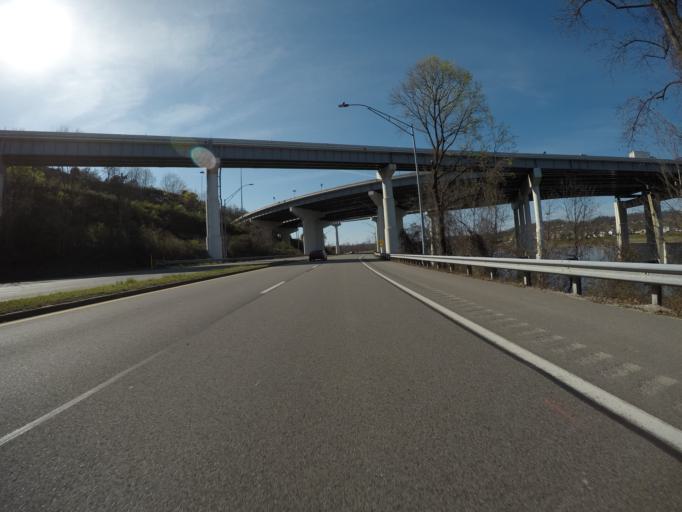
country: US
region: West Virginia
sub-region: Kanawha County
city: Charleston
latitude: 38.3538
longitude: -81.6493
